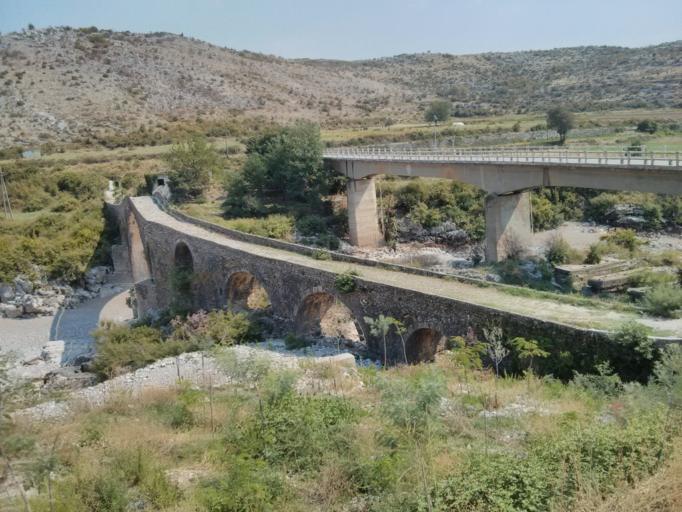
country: AL
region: Shkoder
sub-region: Rrethi i Shkodres
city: Guri i Zi
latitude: 42.1146
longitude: 19.5742
